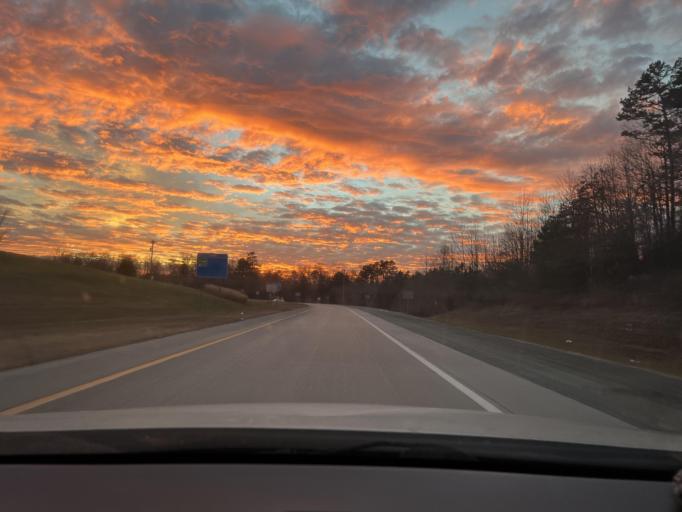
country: US
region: North Carolina
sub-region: Guilford County
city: Forest Oaks
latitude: 36.0254
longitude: -79.7293
